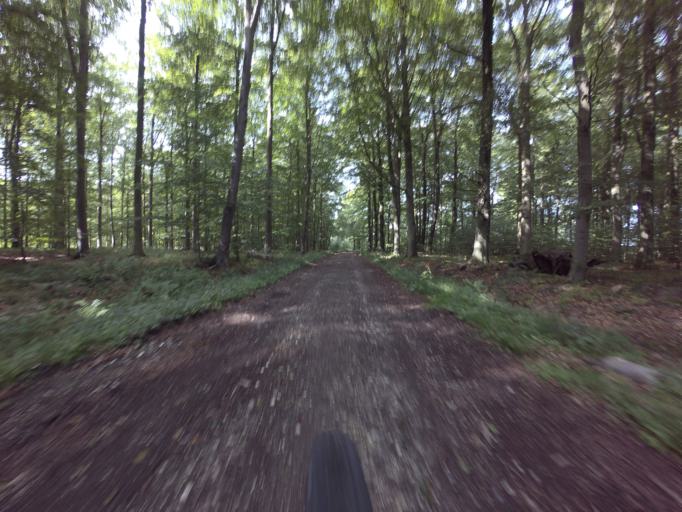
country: DK
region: Zealand
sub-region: Faxe Kommune
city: Fakse Ladeplads
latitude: 55.2355
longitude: 12.2079
